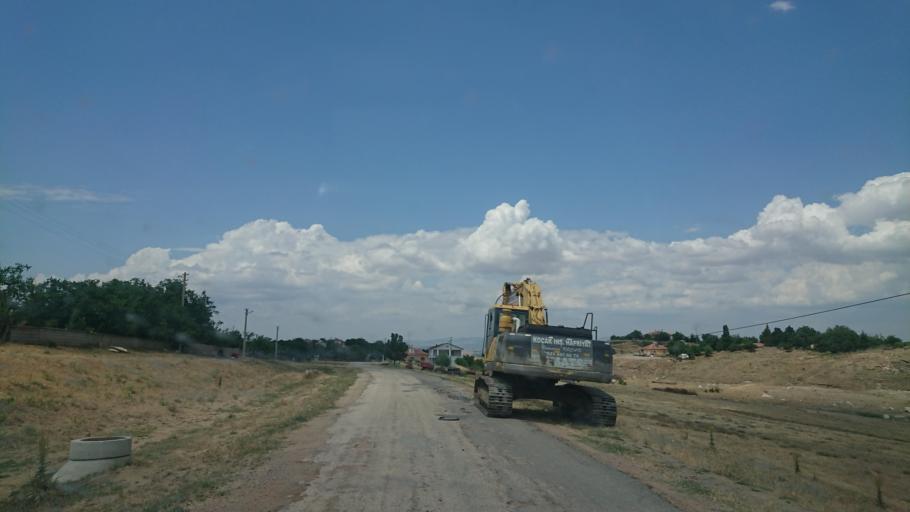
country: TR
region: Aksaray
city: Sariyahsi
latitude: 38.9536
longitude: 33.8832
